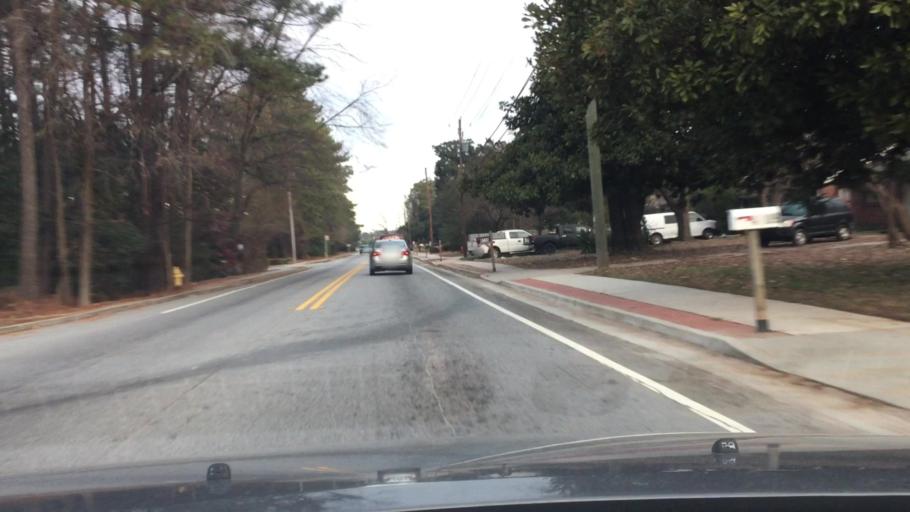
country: US
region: Georgia
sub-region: DeKalb County
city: Doraville
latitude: 33.9329
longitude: -84.2656
